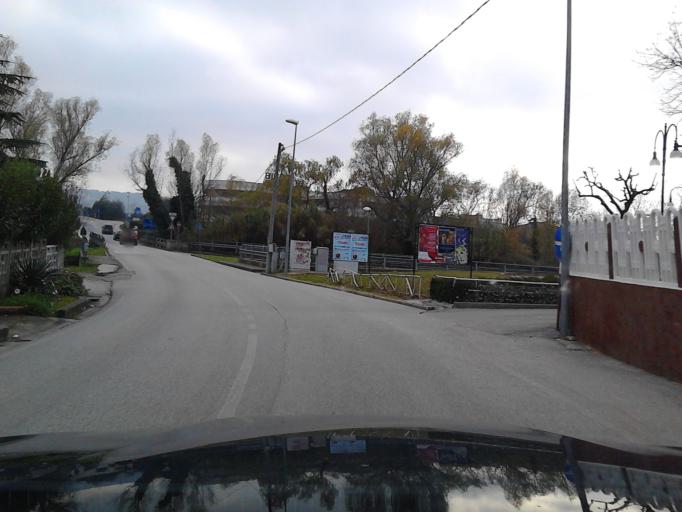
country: IT
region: Abruzzo
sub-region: Provincia di Teramo
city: Villa Rosa
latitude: 42.8349
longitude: 13.8932
